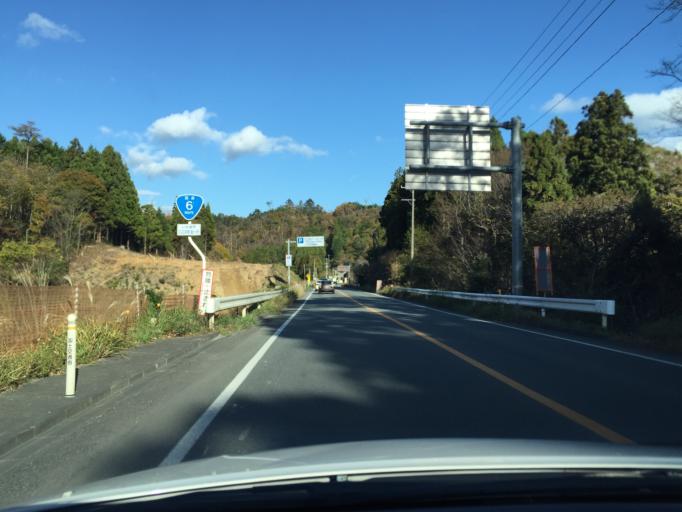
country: JP
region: Fukushima
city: Iwaki
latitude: 37.1582
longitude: 140.9956
